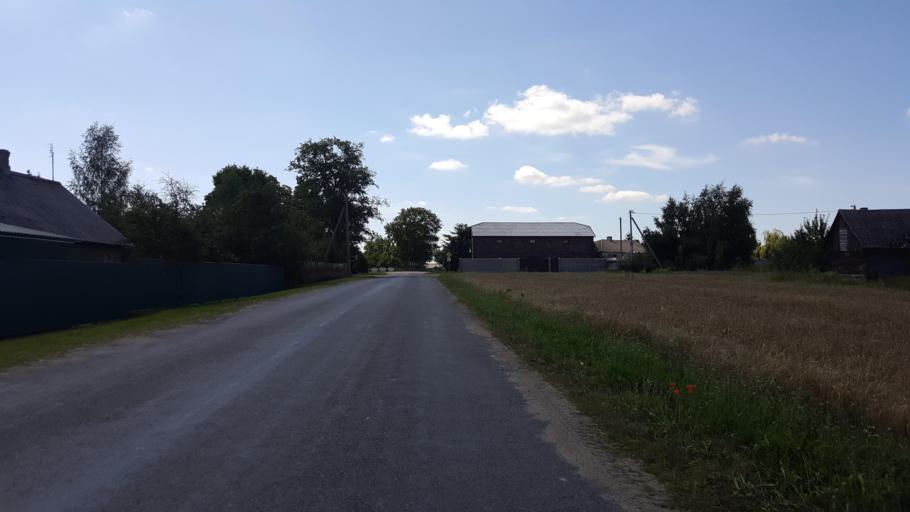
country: BY
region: Brest
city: Charnawchytsy
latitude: 52.3470
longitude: 23.6131
